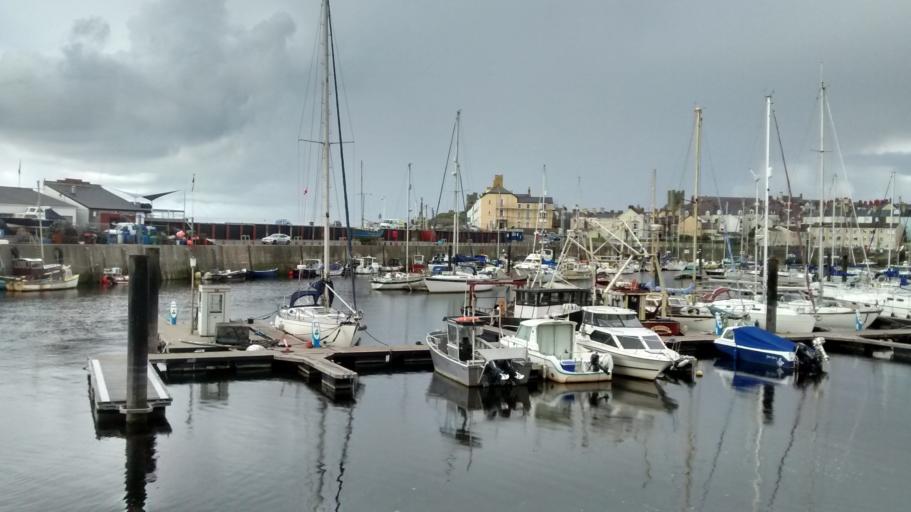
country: GB
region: Wales
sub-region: County of Ceredigion
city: Aberystwyth
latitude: 52.4091
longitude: -4.0878
